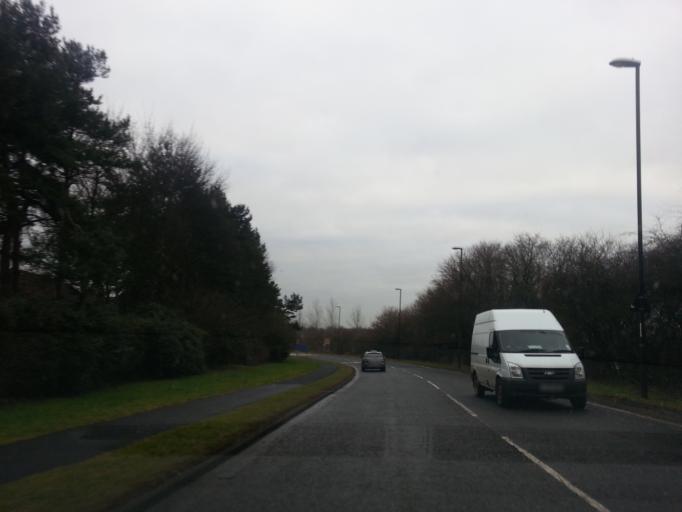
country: GB
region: England
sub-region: County Durham
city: Chester-le-Street
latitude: 54.8786
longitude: -1.5615
